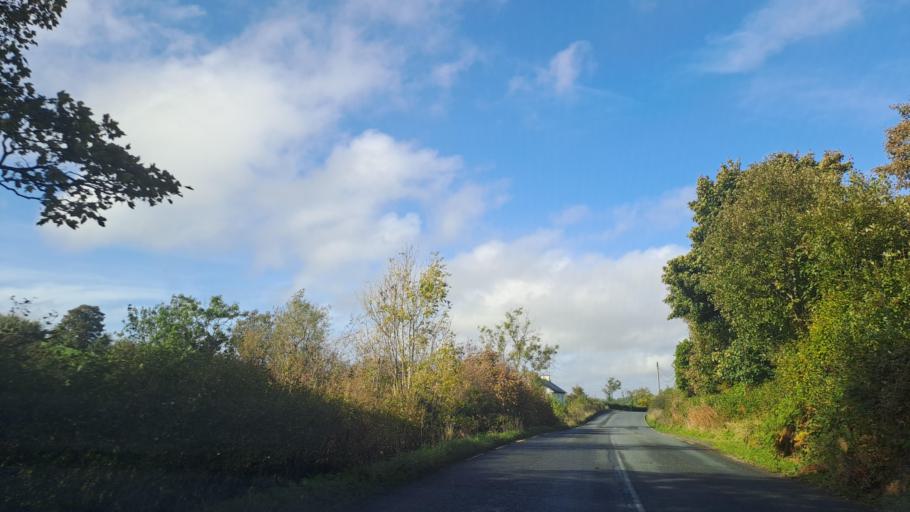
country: IE
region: Ulster
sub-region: An Cabhan
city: Bailieborough
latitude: 54.0230
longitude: -6.9513
